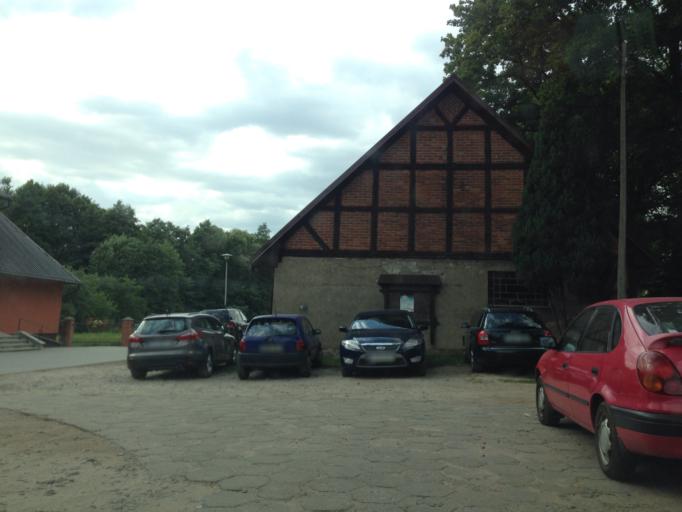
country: PL
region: Kujawsko-Pomorskie
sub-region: Powiat swiecki
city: Bukowiec
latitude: 53.3483
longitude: 18.3107
